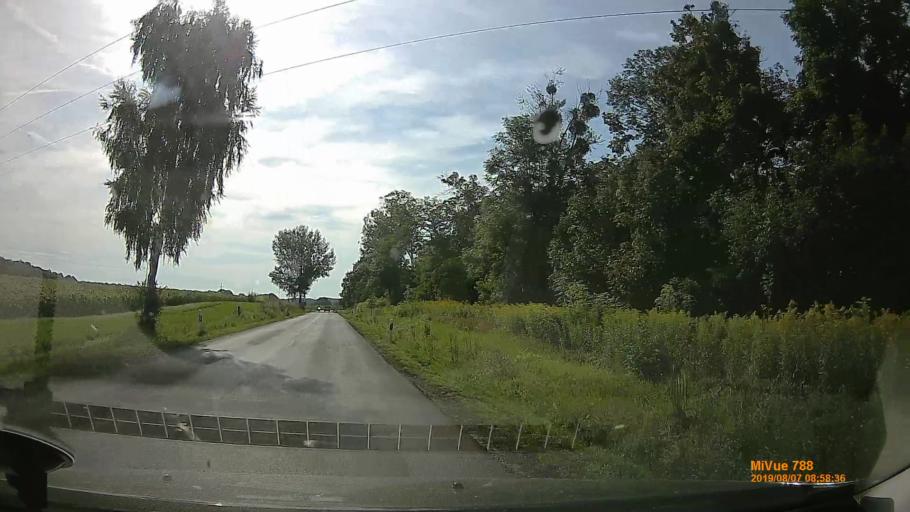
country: HU
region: Zala
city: Pacsa
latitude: 46.7422
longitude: 16.9267
